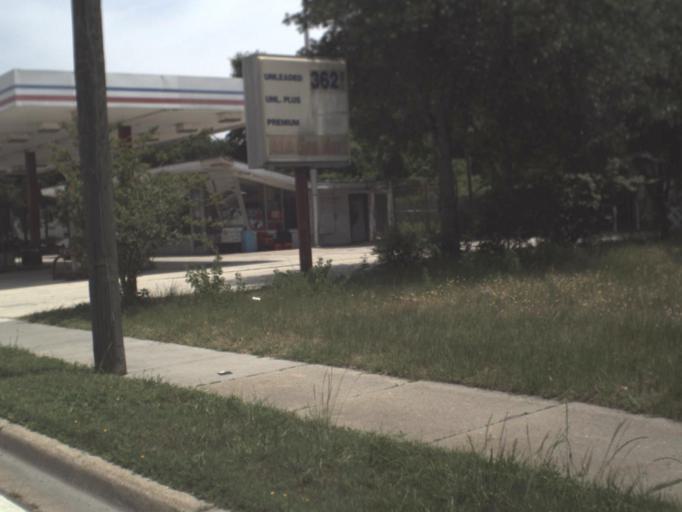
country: US
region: Florida
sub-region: Nassau County
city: Fernandina Beach
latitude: 30.6597
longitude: -81.4604
